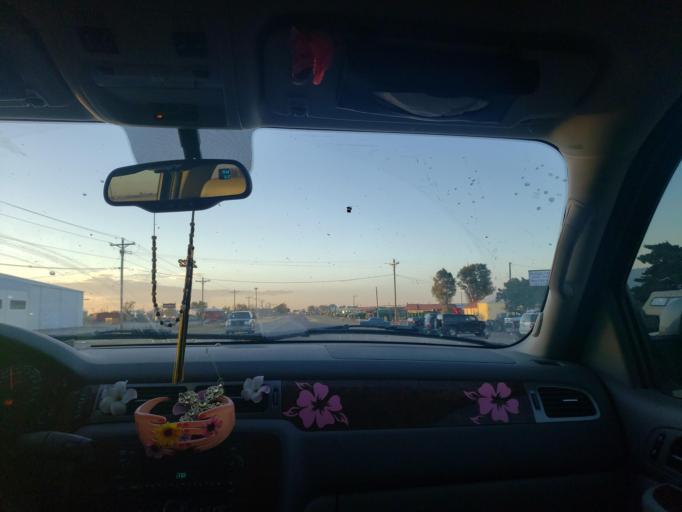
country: US
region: Kansas
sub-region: Finney County
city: Garden City
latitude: 37.9826
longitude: -100.9042
